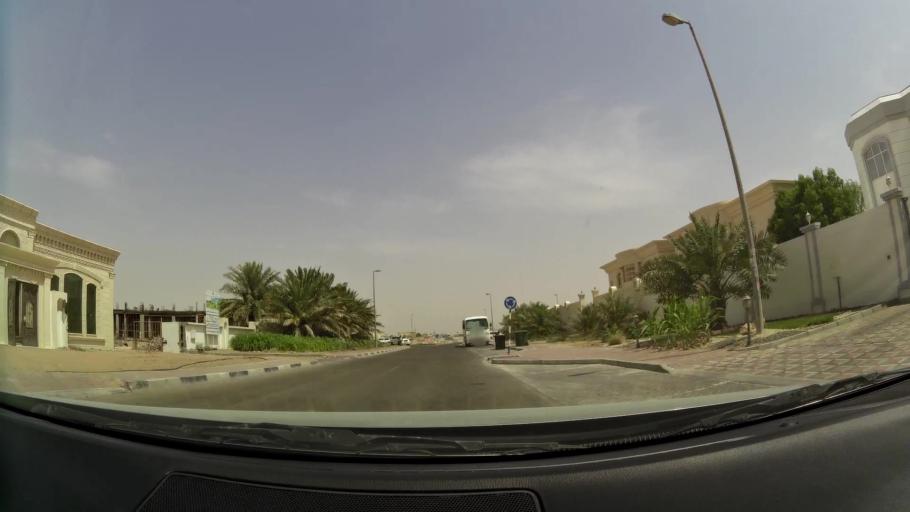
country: AE
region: Abu Dhabi
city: Al Ain
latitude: 24.1832
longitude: 55.7145
